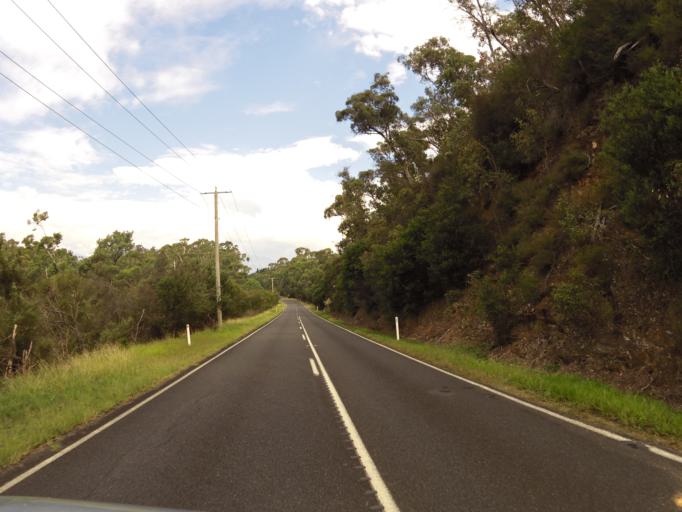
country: AU
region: Victoria
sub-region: Alpine
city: Mount Beauty
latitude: -36.7518
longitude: 147.0177
